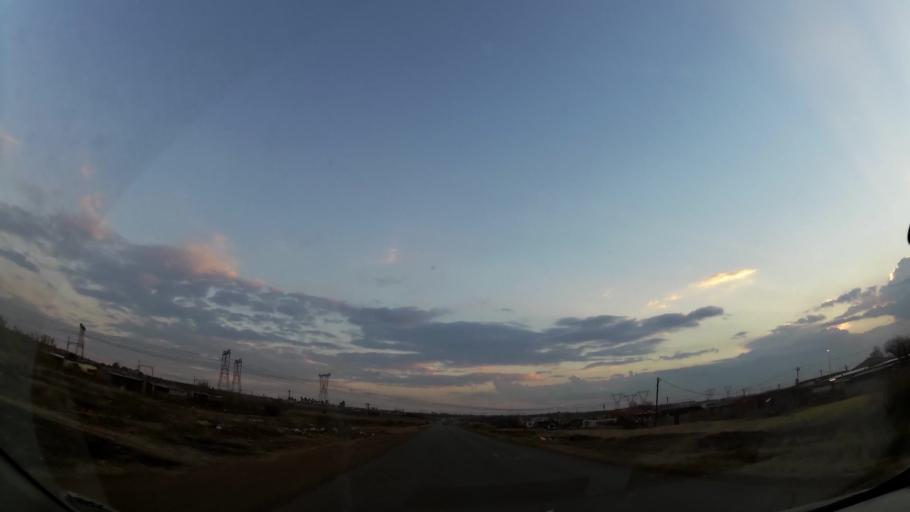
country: ZA
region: Gauteng
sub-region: City of Johannesburg Metropolitan Municipality
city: Orange Farm
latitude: -26.5597
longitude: 27.8751
